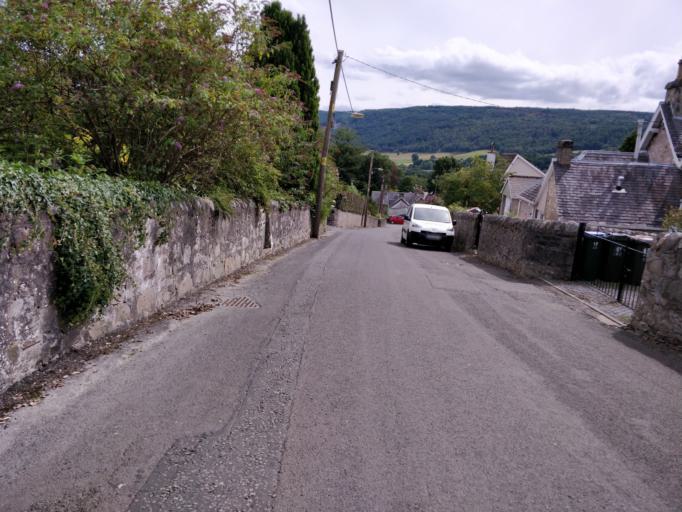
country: GB
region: Scotland
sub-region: Perth and Kinross
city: Pitlochry
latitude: 56.7054
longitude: -3.7286
